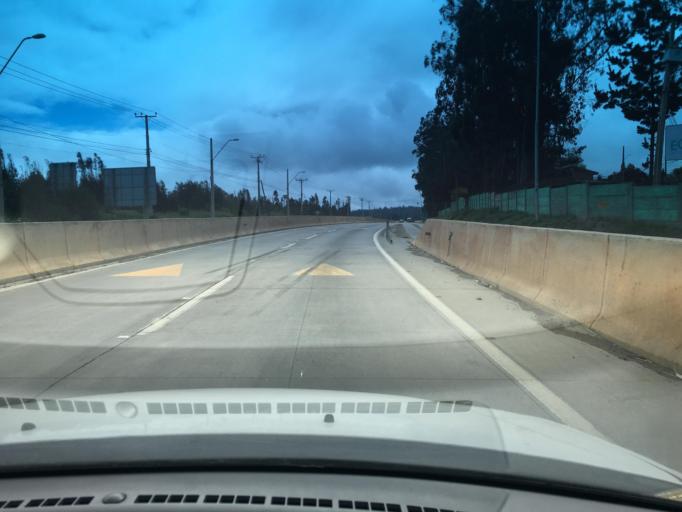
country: CL
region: Valparaiso
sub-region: Provincia de Valparaiso
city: Valparaiso
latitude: -33.0960
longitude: -71.5874
